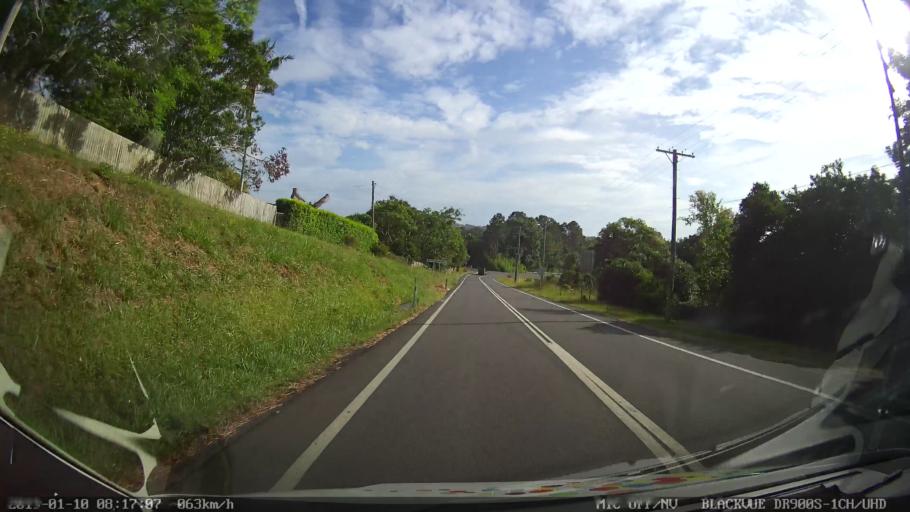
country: AU
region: New South Wales
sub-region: Bellingen
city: Bellingen
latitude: -30.4701
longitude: 152.9388
